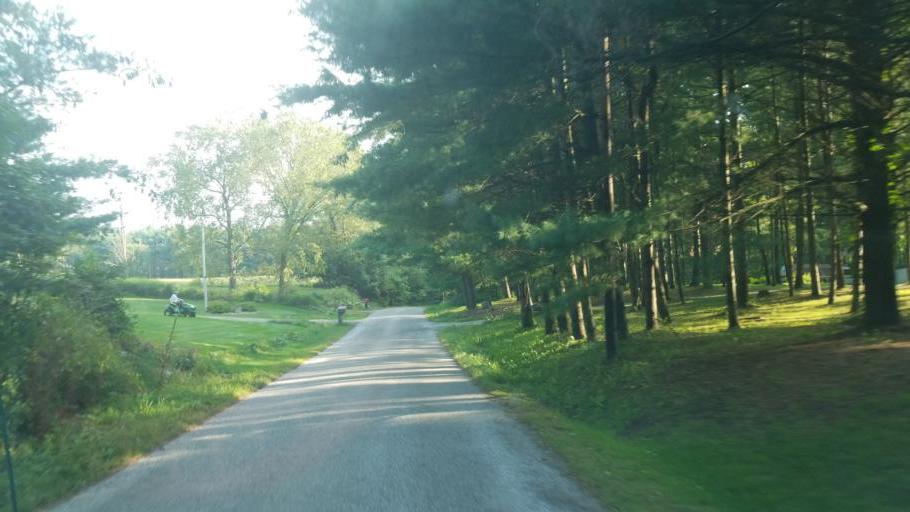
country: US
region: Ohio
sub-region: Wayne County
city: Wooster
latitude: 40.8758
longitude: -82.0235
